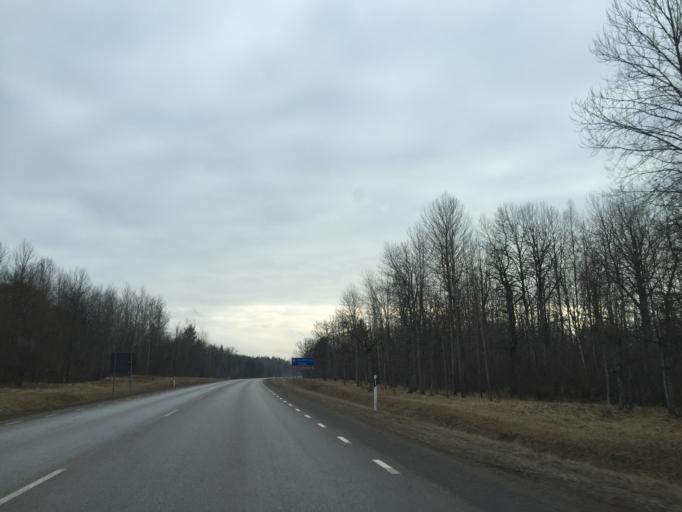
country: EE
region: Saare
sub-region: Orissaare vald
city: Orissaare
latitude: 58.4638
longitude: 22.8133
